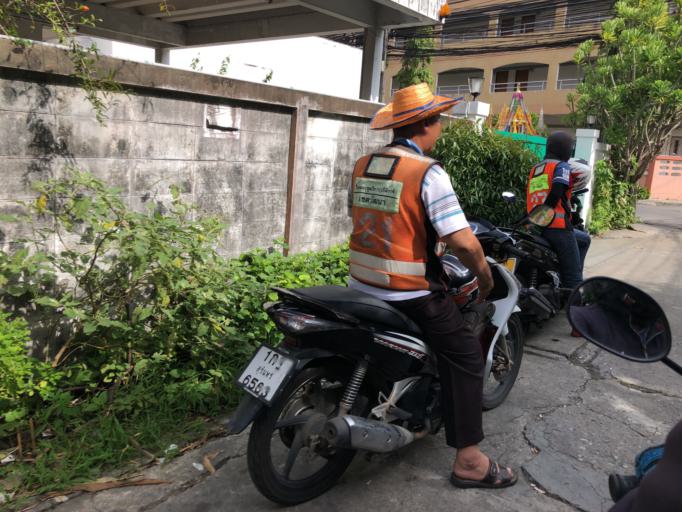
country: TH
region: Bangkok
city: Watthana
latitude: 13.7198
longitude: 100.6001
